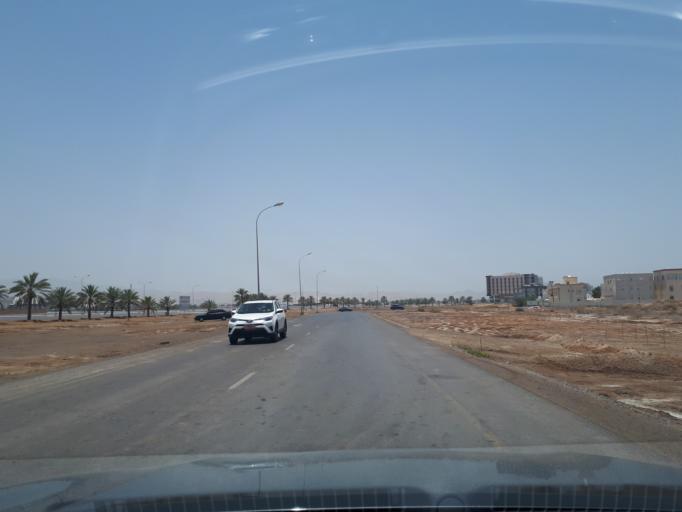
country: OM
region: Muhafazat Masqat
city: As Sib al Jadidah
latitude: 23.6240
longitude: 58.2625
